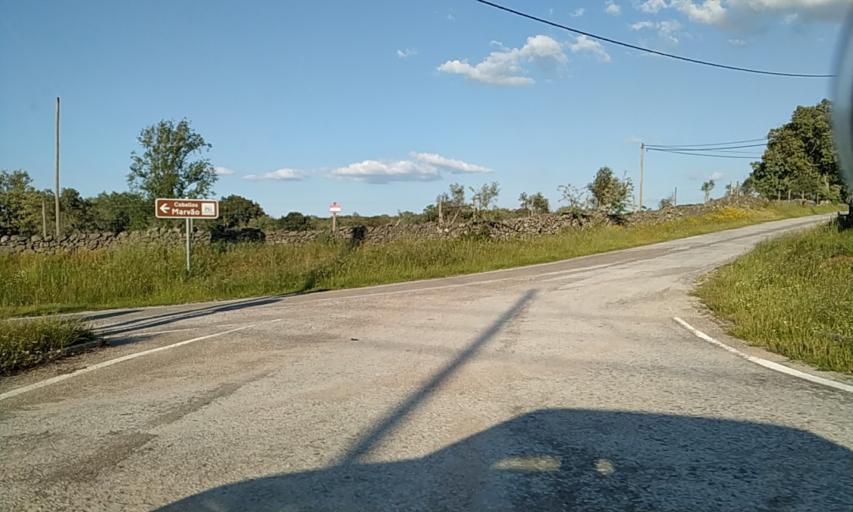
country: PT
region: Portalegre
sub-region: Portalegre
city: Reguengo
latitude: 39.3461
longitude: -7.4076
